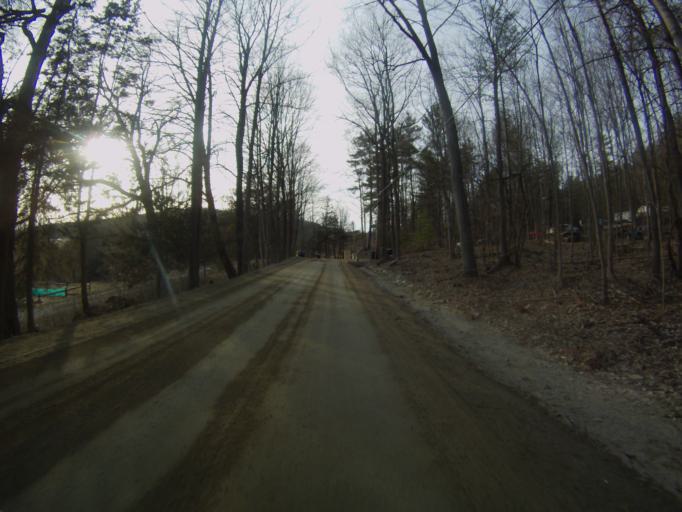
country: US
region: Vermont
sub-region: Addison County
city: Middlebury (village)
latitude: 44.0320
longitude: -73.2665
